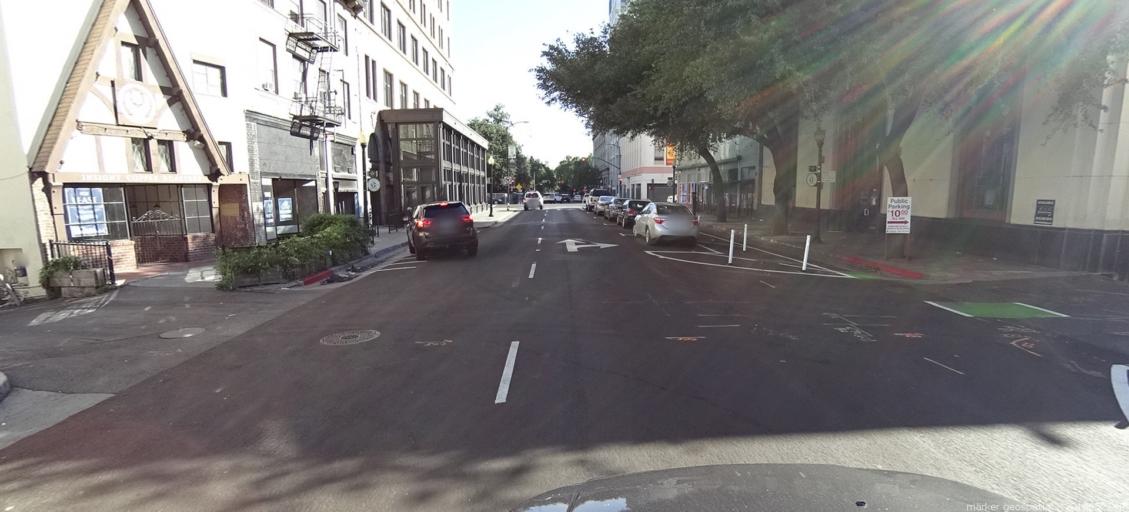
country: US
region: California
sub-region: Sacramento County
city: Sacramento
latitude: 38.5797
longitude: -121.4938
